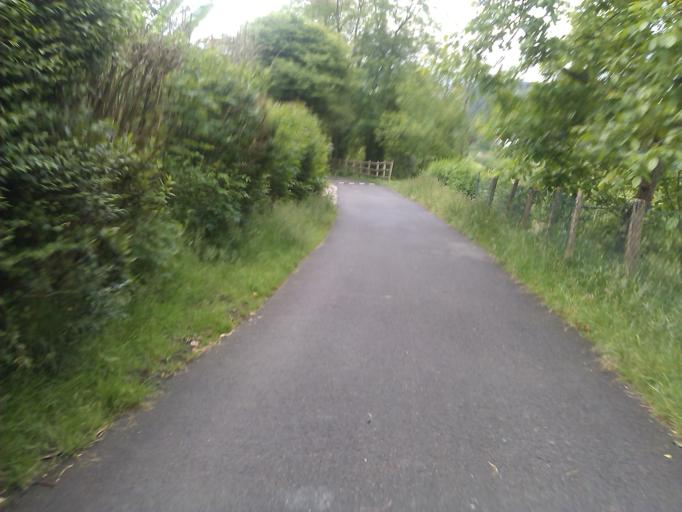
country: ES
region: Basque Country
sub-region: Provincia de Guipuzcoa
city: Andoain
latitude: 43.2107
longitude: -2.0130
